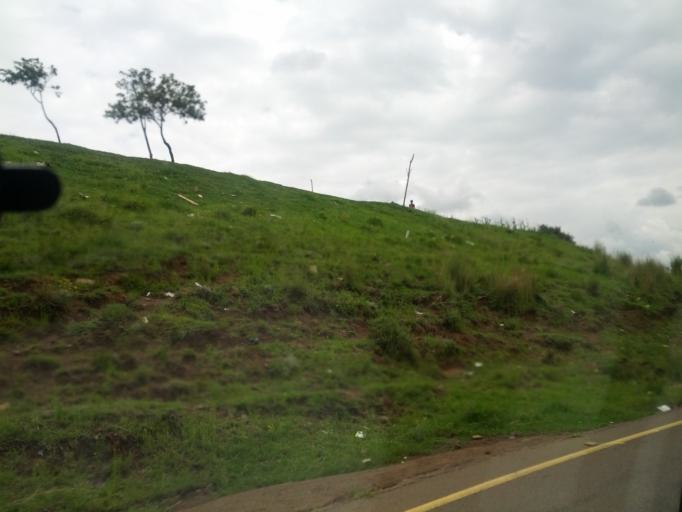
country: LS
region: Butha-Buthe
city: Butha-Buthe
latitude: -29.0356
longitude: 28.2871
